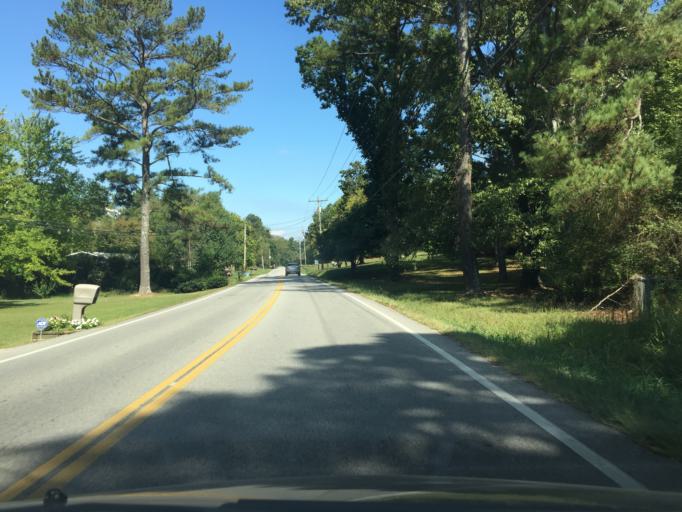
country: US
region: Tennessee
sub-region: Hamilton County
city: Collegedale
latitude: 35.0905
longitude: -85.0787
